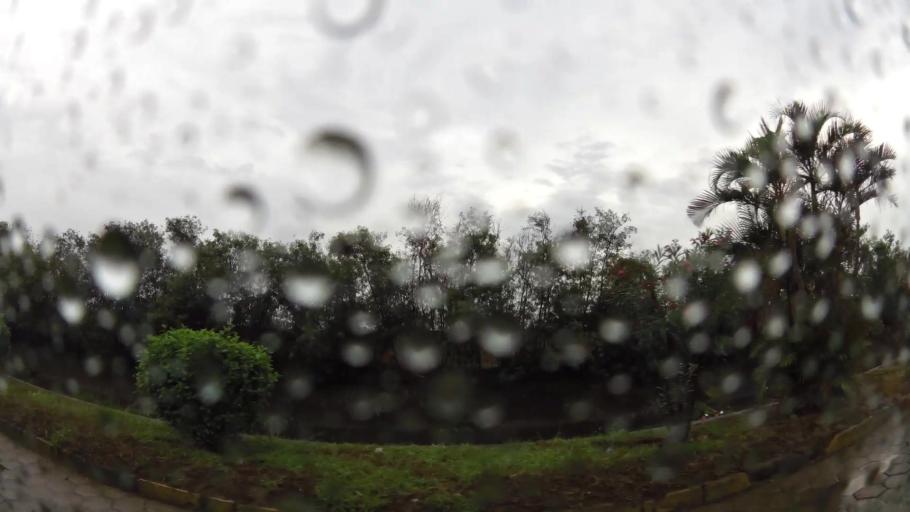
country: BO
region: Santa Cruz
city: Santa Cruz de la Sierra
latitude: -17.7755
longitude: -63.1450
